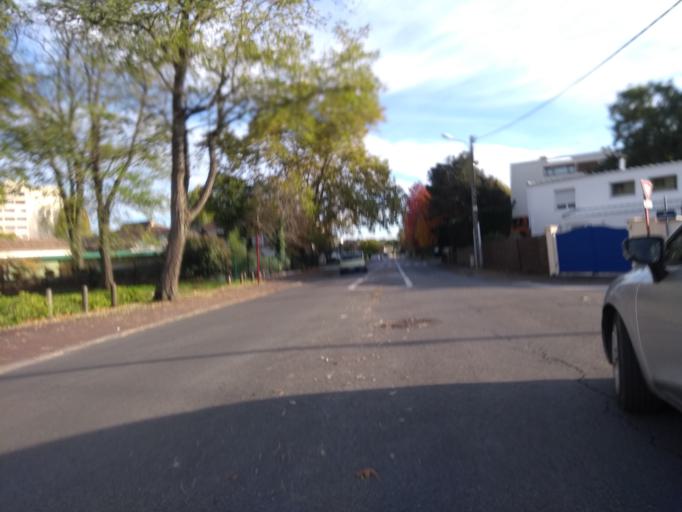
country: FR
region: Aquitaine
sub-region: Departement de la Gironde
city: Pessac
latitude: 44.7917
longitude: -0.6410
